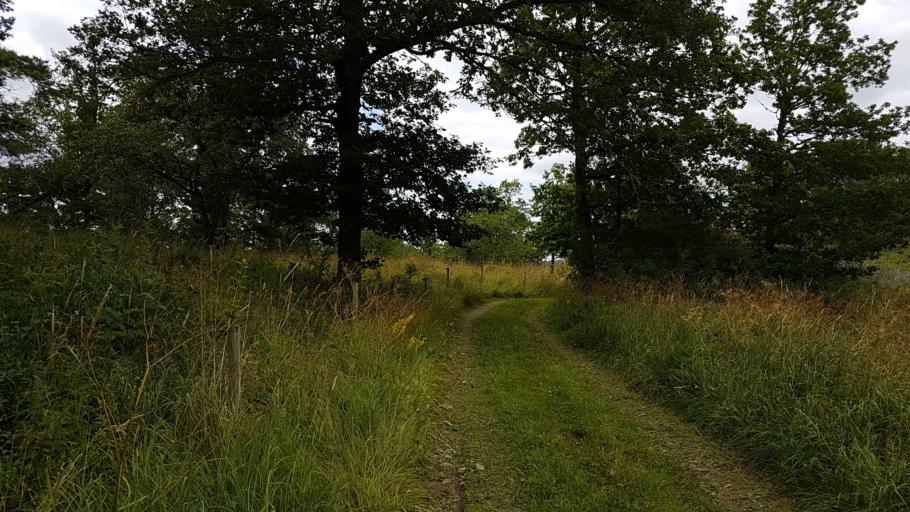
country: SE
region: OEstergoetland
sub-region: Valdemarsviks Kommun
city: Gusum
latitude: 58.4311
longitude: 16.5695
